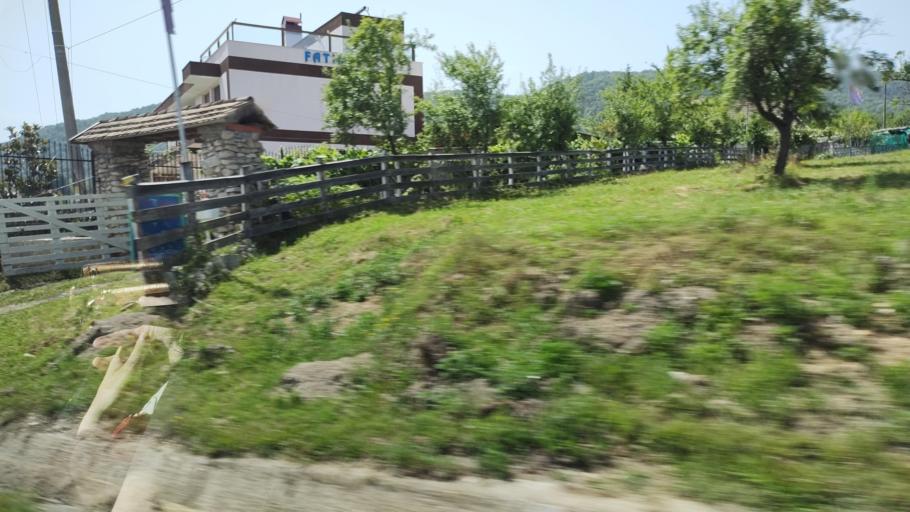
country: RO
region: Mehedinti
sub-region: Comuna Eselnita
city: Eselnita
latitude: 44.6832
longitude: 22.3436
